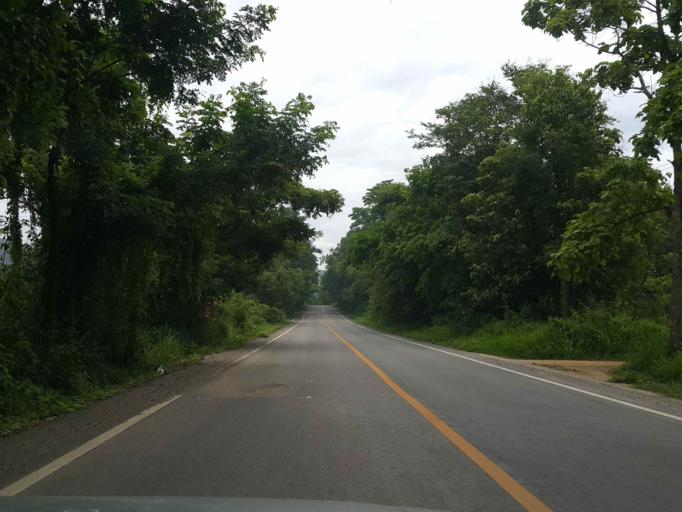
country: TH
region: Lampang
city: Thoen
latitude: 17.5617
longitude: 99.3327
